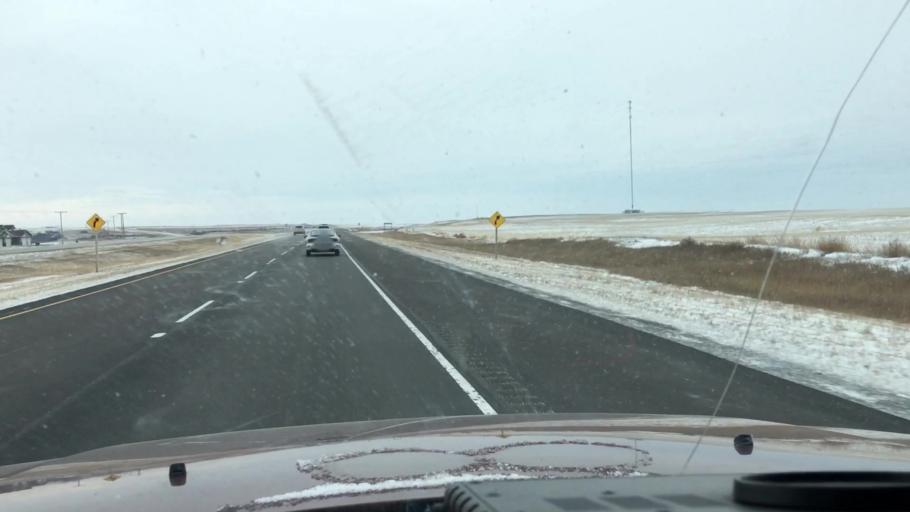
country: CA
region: Saskatchewan
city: Saskatoon
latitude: 51.7429
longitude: -106.4763
